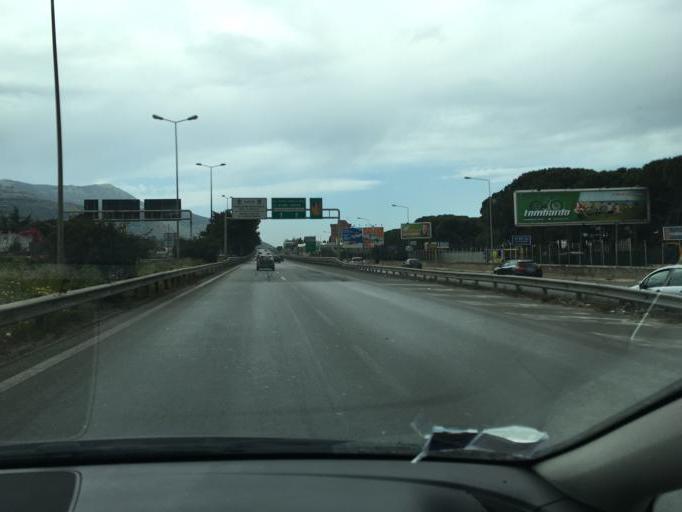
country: IT
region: Sicily
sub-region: Palermo
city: Palermo
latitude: 38.1518
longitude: 13.3226
